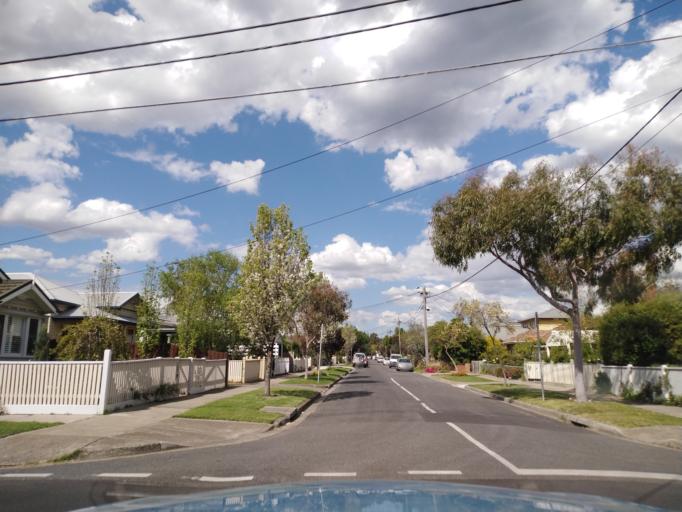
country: AU
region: Victoria
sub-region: Hobsons Bay
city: Newport
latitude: -37.8441
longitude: 144.8765
